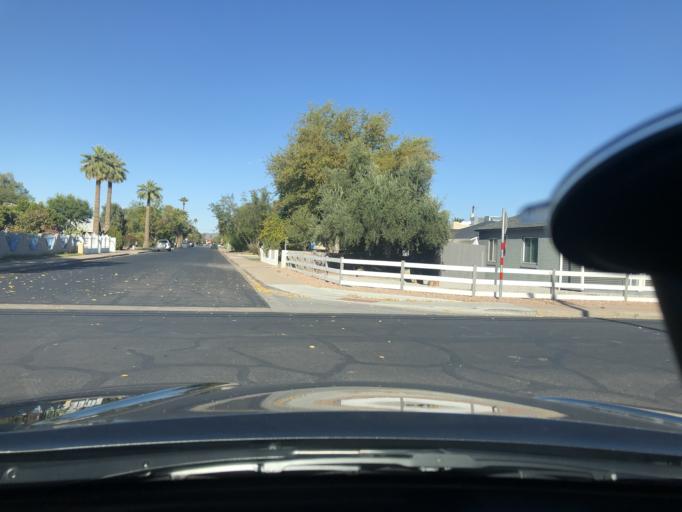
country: US
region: Arizona
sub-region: Maricopa County
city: Phoenix
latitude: 33.4711
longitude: -112.0324
